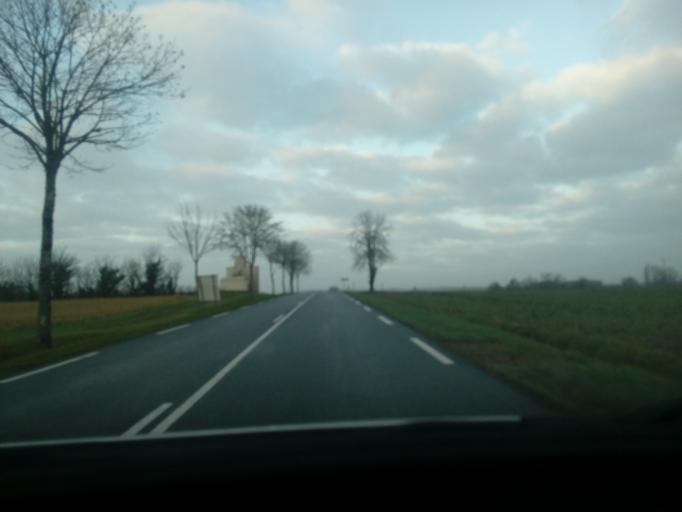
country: FR
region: Poitou-Charentes
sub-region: Departement de la Charente
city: Baignes-Sainte-Radegonde
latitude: 45.4436
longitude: -0.3112
